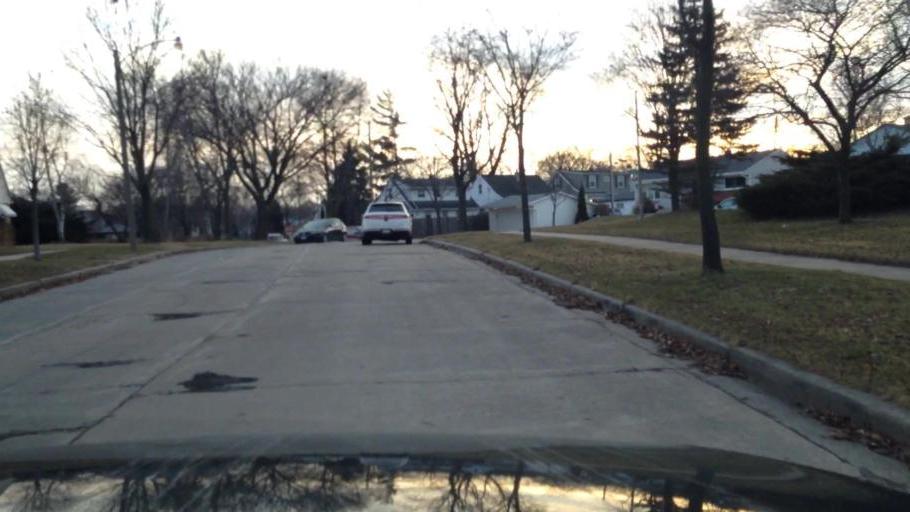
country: US
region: Wisconsin
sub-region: Milwaukee County
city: West Milwaukee
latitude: 42.9968
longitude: -87.9908
